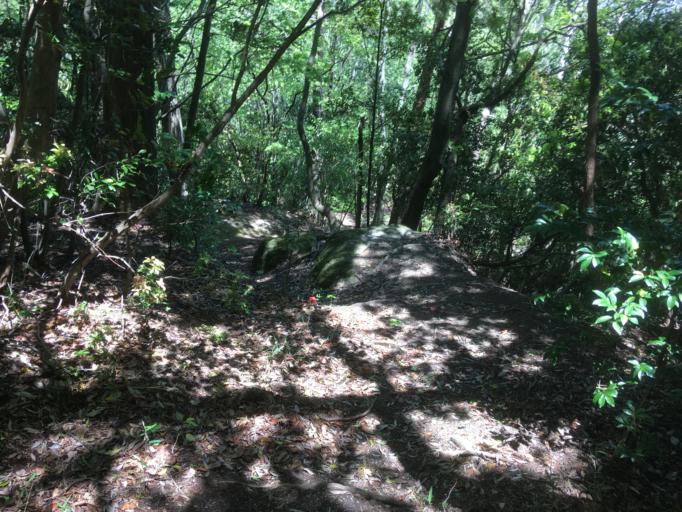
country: JP
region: Nara
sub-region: Ikoma-shi
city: Ikoma
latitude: 34.6927
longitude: 135.6884
